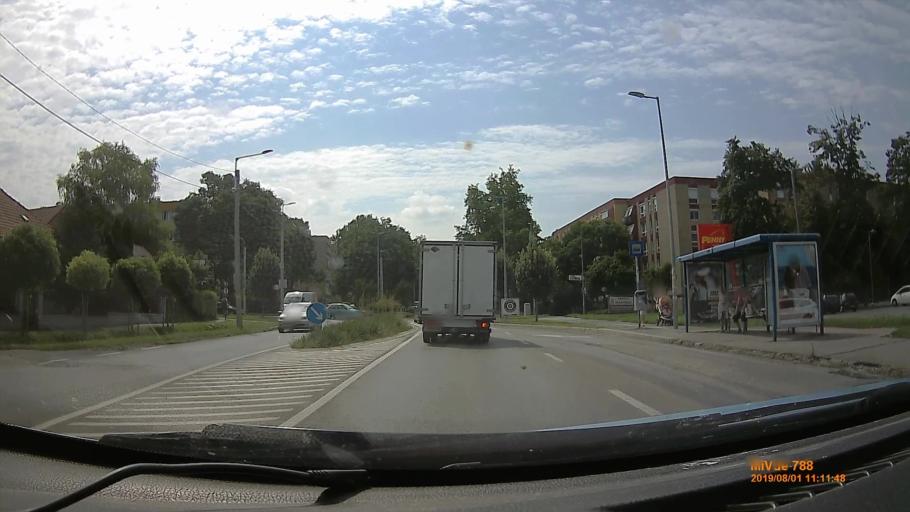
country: HU
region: Baranya
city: Pecs
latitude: 46.0473
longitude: 18.2143
